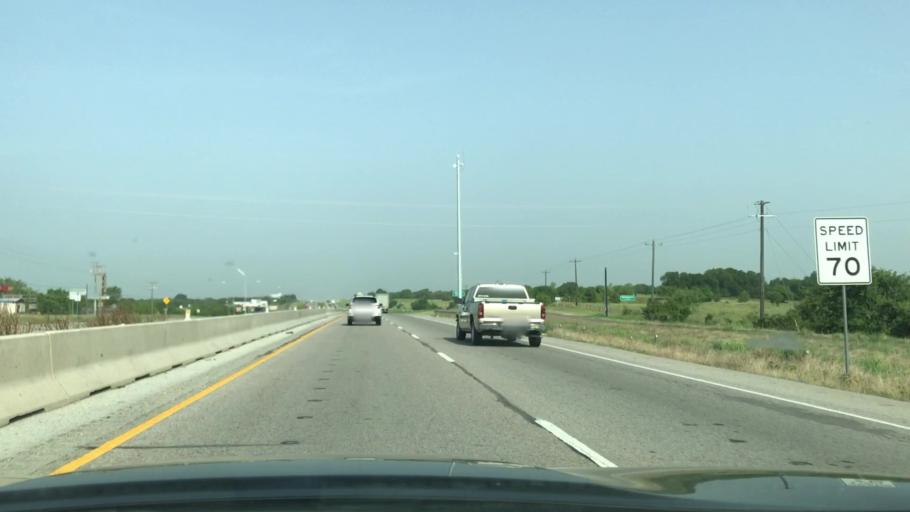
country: US
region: Texas
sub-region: Dallas County
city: Sunnyvale
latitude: 32.7776
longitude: -96.5183
